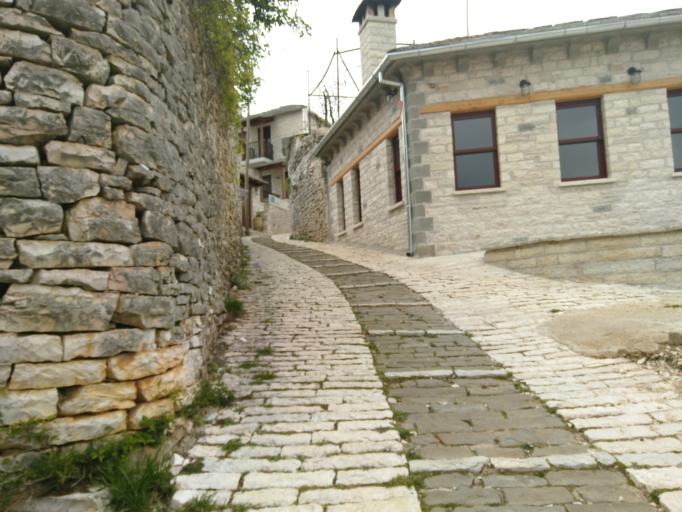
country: GR
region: Epirus
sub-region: Nomos Ioanninon
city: Asprangeloi
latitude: 39.8822
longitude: 20.7463
